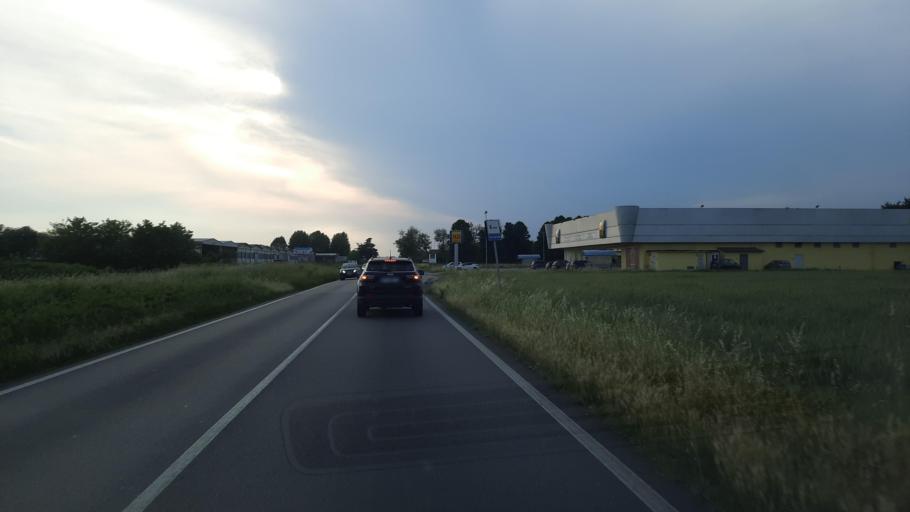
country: IT
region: Lombardy
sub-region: Provincia di Pavia
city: Villanova d'Ardenghi
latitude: 45.1633
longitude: 9.0243
